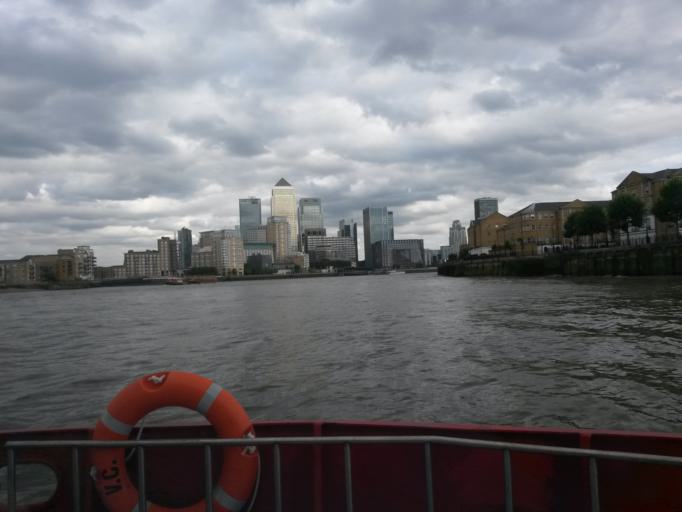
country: GB
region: England
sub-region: Greater London
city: Poplar
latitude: 51.5079
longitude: -0.0385
